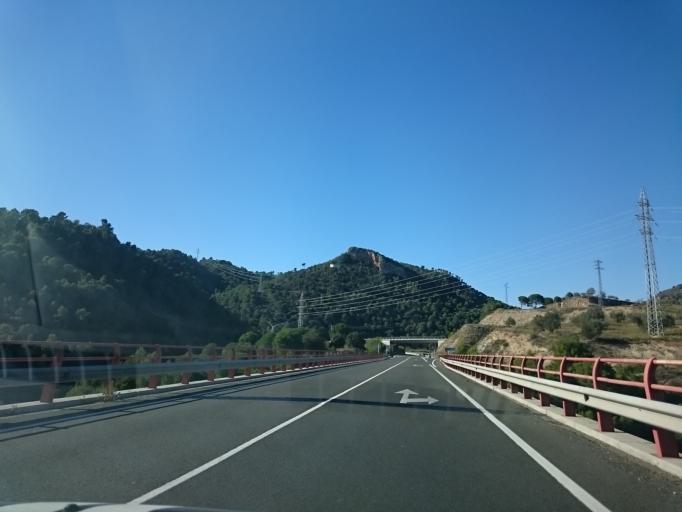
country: ES
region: Catalonia
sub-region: Provincia de Barcelona
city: Capellades
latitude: 41.5113
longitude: 1.7009
